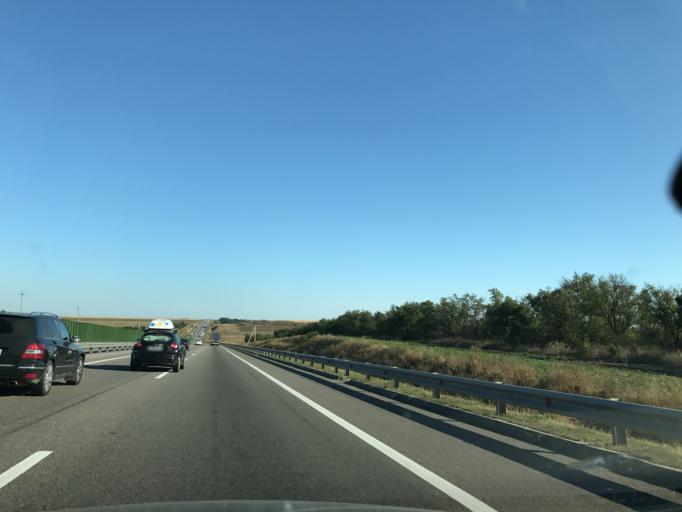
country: RU
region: Rostov
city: Glubokiy
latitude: 48.5977
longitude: 40.3537
